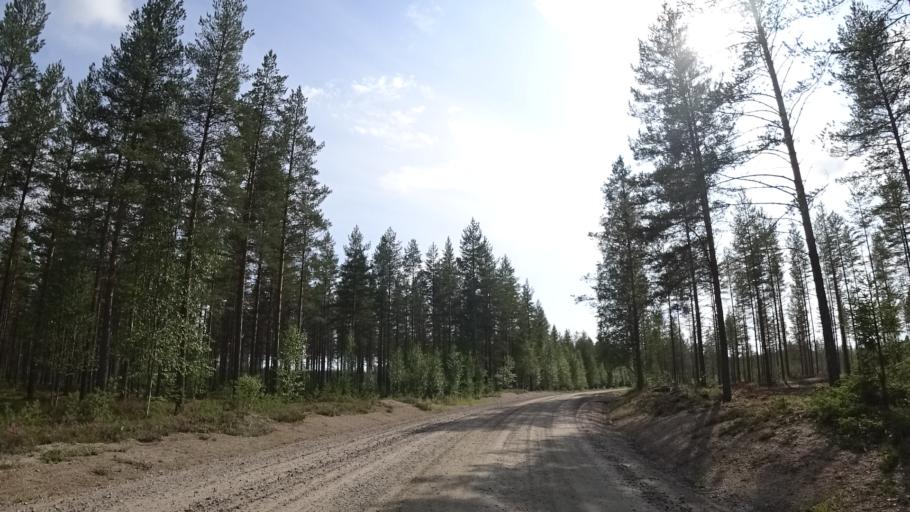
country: FI
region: North Karelia
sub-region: Pielisen Karjala
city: Lieksa
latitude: 63.5459
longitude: 30.0585
